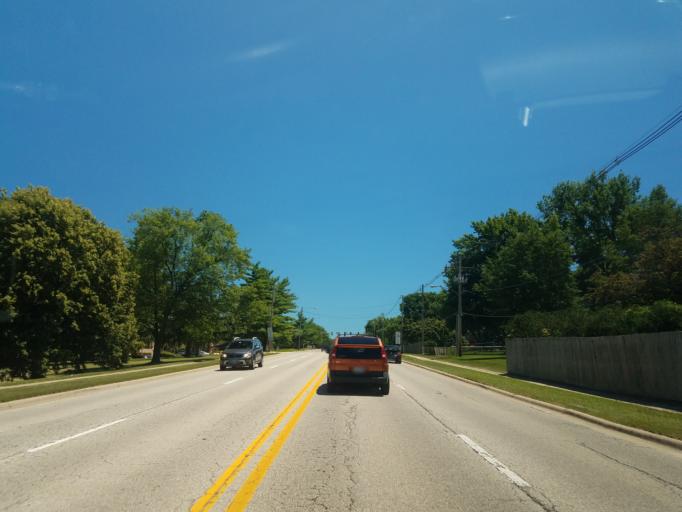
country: US
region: Illinois
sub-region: McLean County
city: Normal
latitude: 40.5103
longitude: -88.9712
